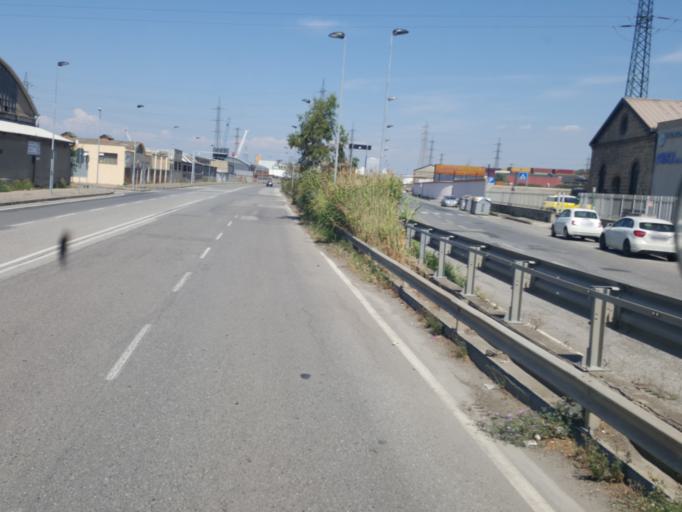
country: IT
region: Tuscany
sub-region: Provincia di Livorno
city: Livorno
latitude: 43.5663
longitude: 10.3131
